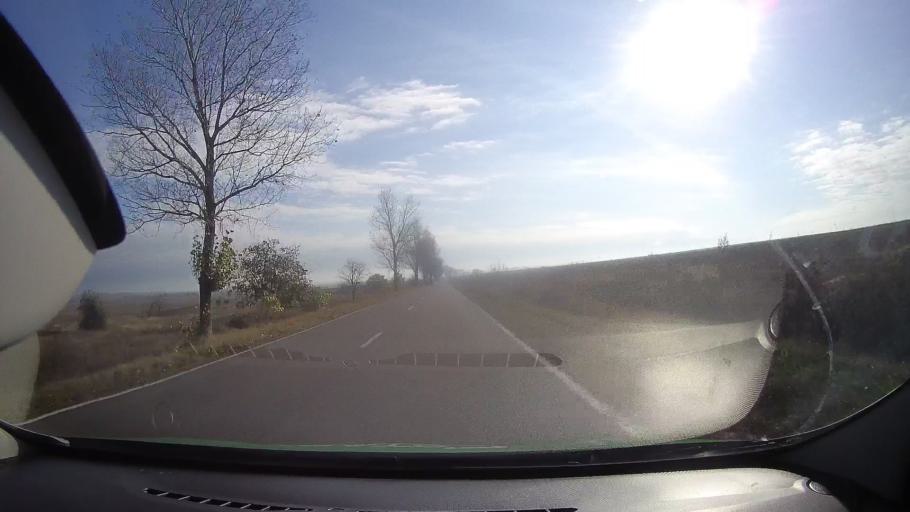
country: RO
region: Tulcea
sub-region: Comuna Mahmudia
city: Mahmudia
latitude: 45.0705
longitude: 29.0974
